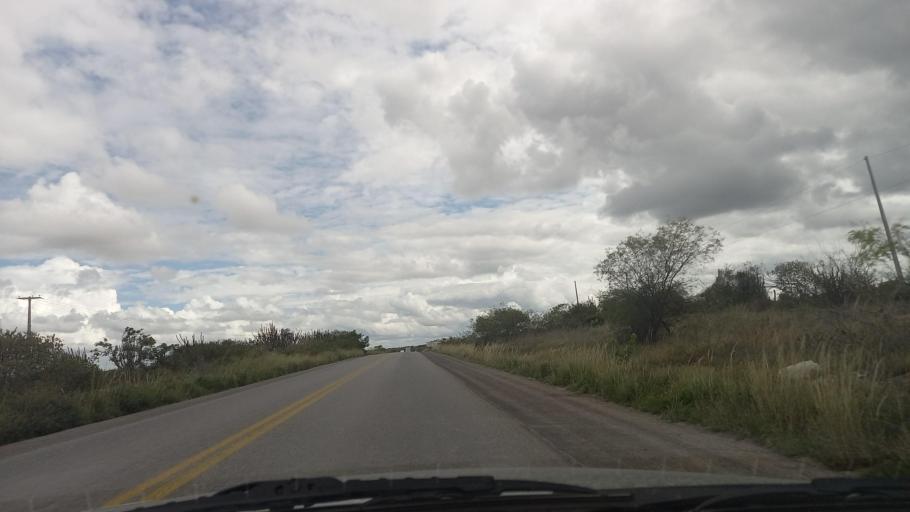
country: BR
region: Pernambuco
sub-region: Cachoeirinha
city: Cachoeirinha
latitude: -8.3456
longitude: -36.1650
